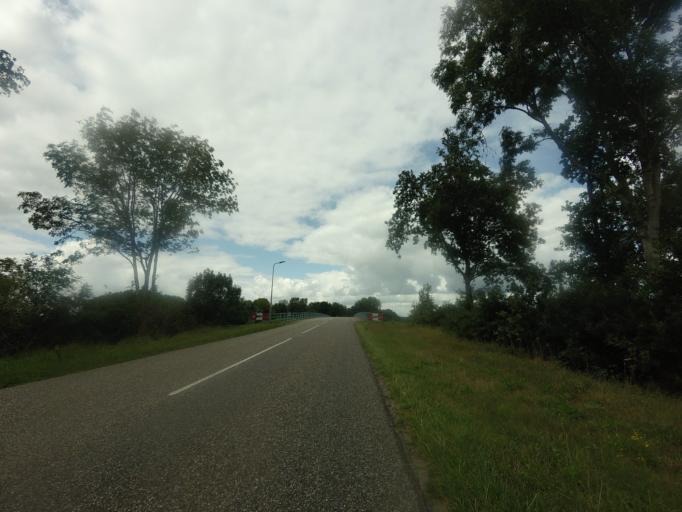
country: NL
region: Drenthe
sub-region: Gemeente Meppel
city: Meppel
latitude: 52.6798
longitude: 6.2164
